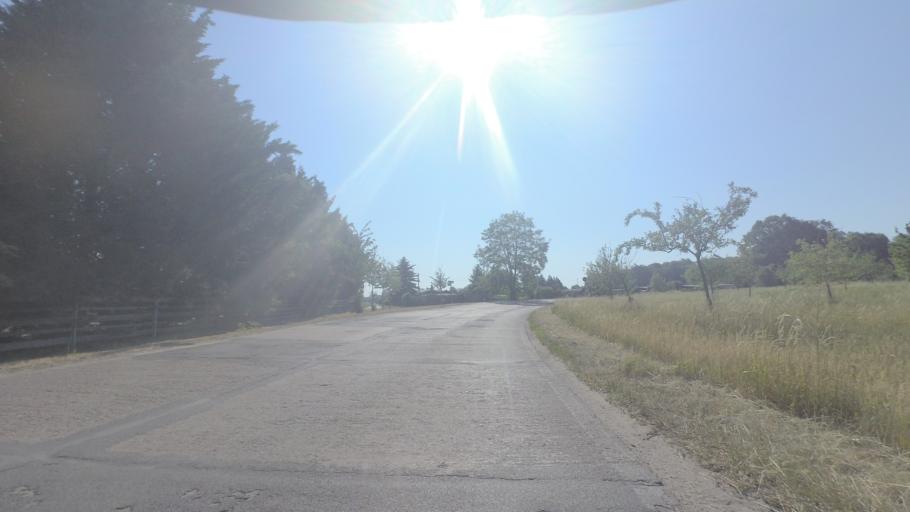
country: DE
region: Saxony-Anhalt
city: Quellendorf
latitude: 51.8165
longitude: 12.1443
